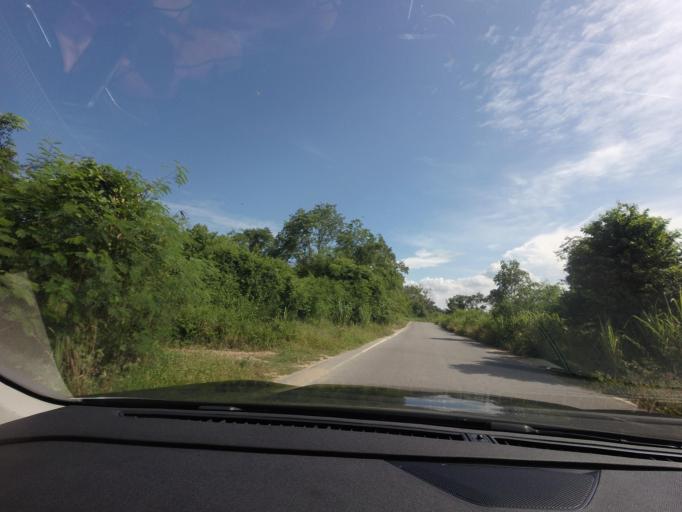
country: TH
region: Prachuap Khiri Khan
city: Hua Hin
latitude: 12.4896
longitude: 99.9426
